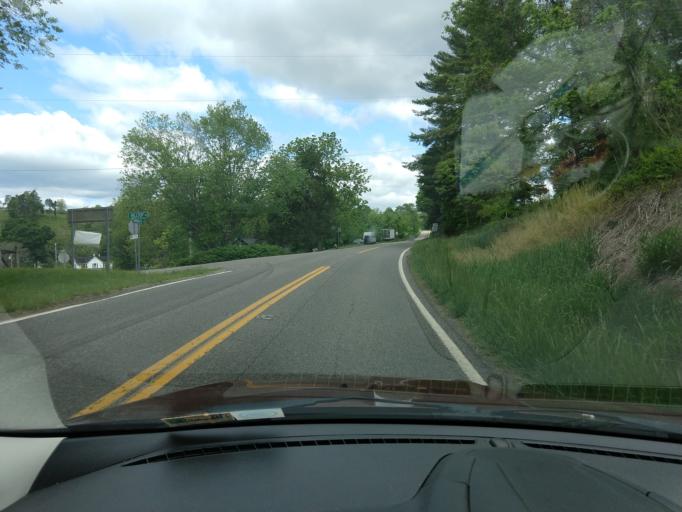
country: US
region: Virginia
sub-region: Wythe County
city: Wytheville
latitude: 36.8398
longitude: -80.9668
